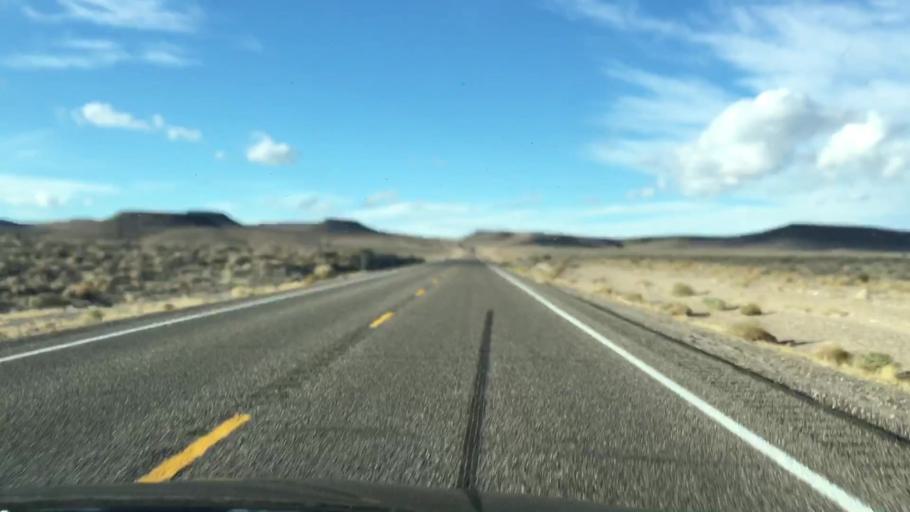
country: US
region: Nevada
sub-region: Esmeralda County
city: Goldfield
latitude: 37.3689
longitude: -117.1245
